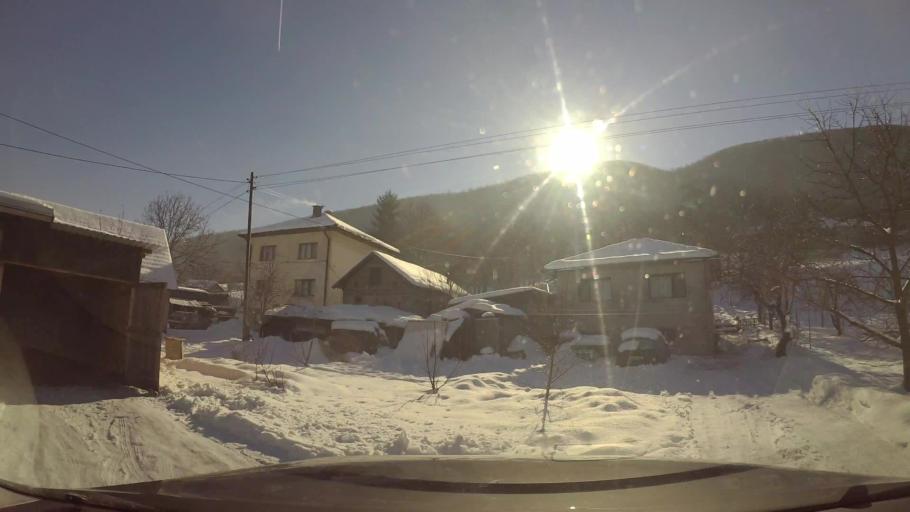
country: BA
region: Federation of Bosnia and Herzegovina
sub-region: Kanton Sarajevo
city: Sarajevo
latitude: 43.7885
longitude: 18.3407
